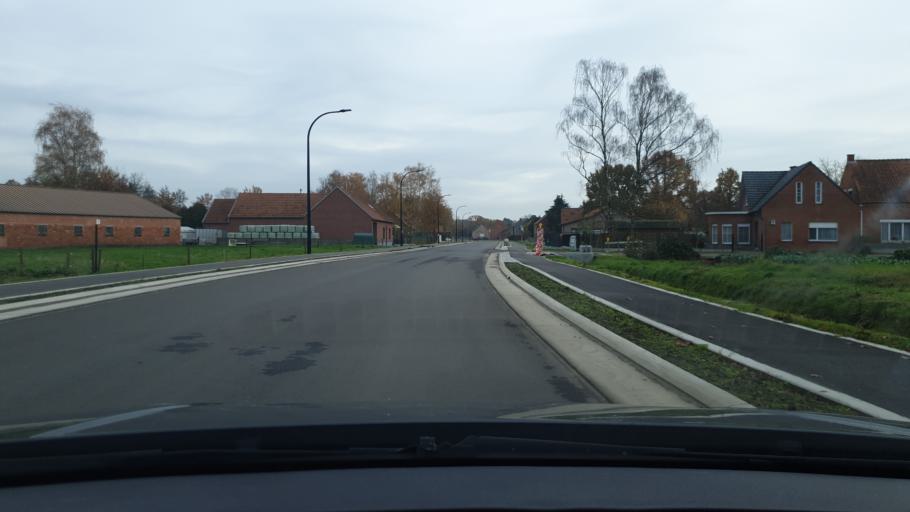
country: BE
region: Flanders
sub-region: Provincie Antwerpen
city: Meerhout
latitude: 51.1263
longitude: 5.0391
